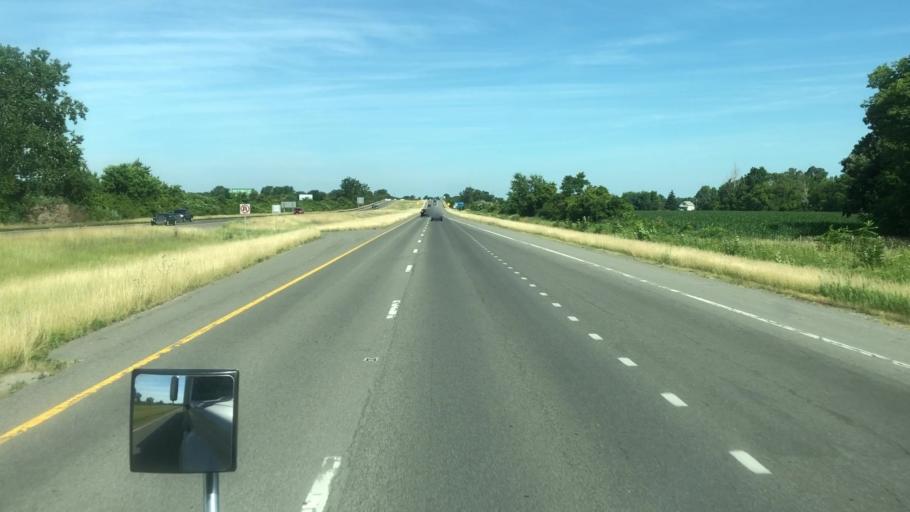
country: US
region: Ohio
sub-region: Erie County
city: Sandusky
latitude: 41.4226
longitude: -82.7636
